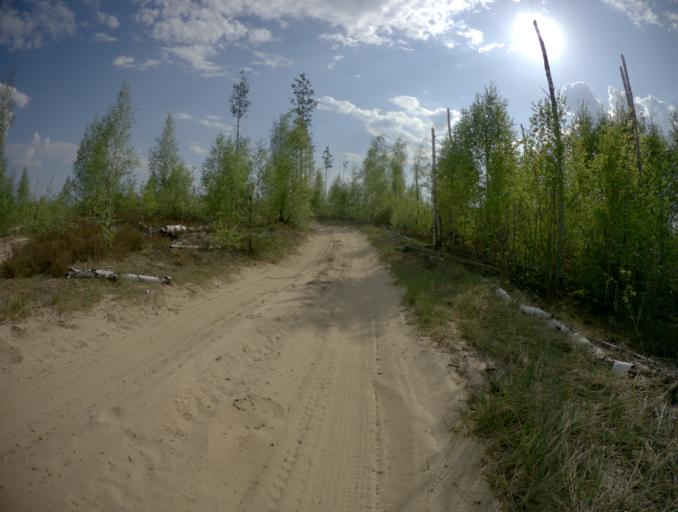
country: RU
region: Ivanovo
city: Talitsy
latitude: 56.4202
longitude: 42.2779
